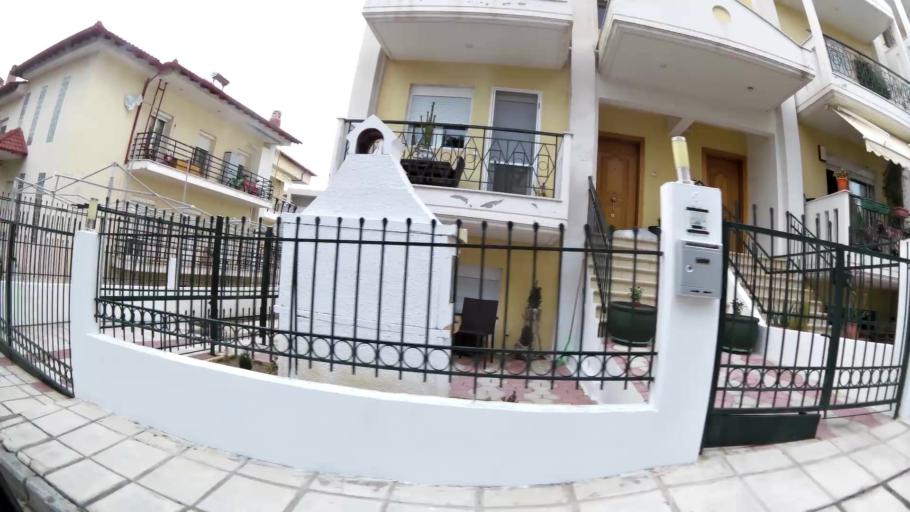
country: GR
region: Central Macedonia
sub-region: Nomos Thessalonikis
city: Oraiokastro
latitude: 40.7114
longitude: 22.9310
